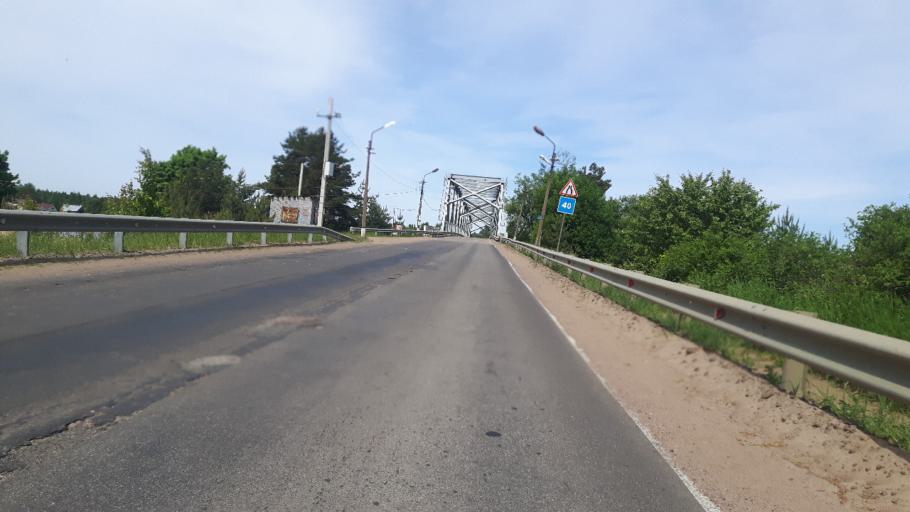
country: RU
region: Leningrad
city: Ust'-Luga
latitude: 59.6513
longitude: 28.2598
